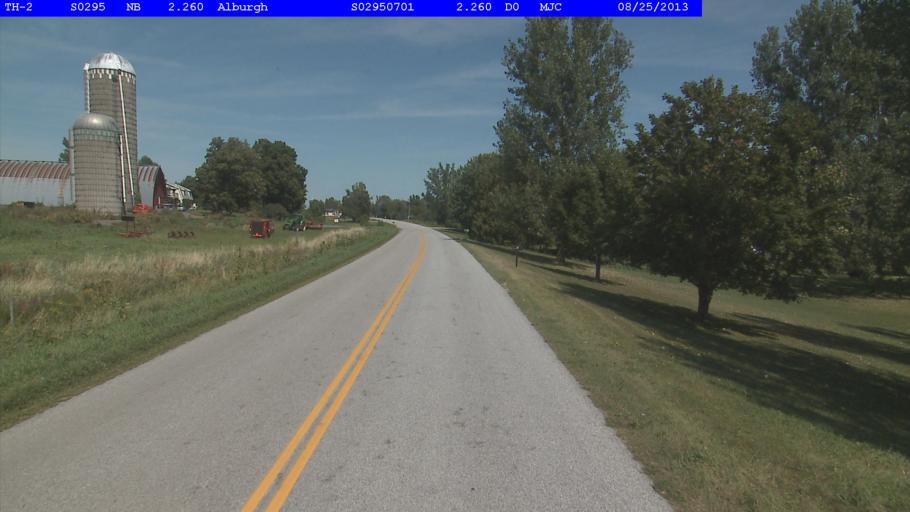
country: US
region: Vermont
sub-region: Franklin County
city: Swanton
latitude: 45.0046
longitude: -73.2150
